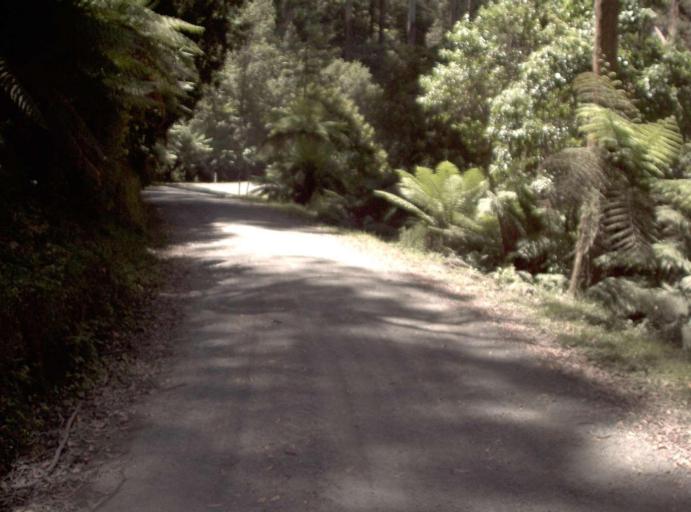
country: AU
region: Victoria
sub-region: Yarra Ranges
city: Millgrove
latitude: -37.6966
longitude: 145.7210
